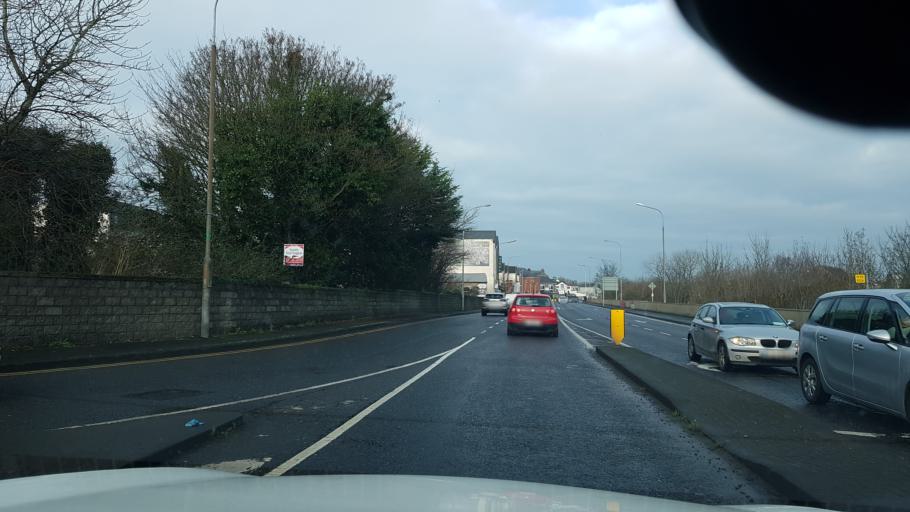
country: IE
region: Leinster
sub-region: An Mhi
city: Navan
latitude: 53.6509
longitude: -6.6809
